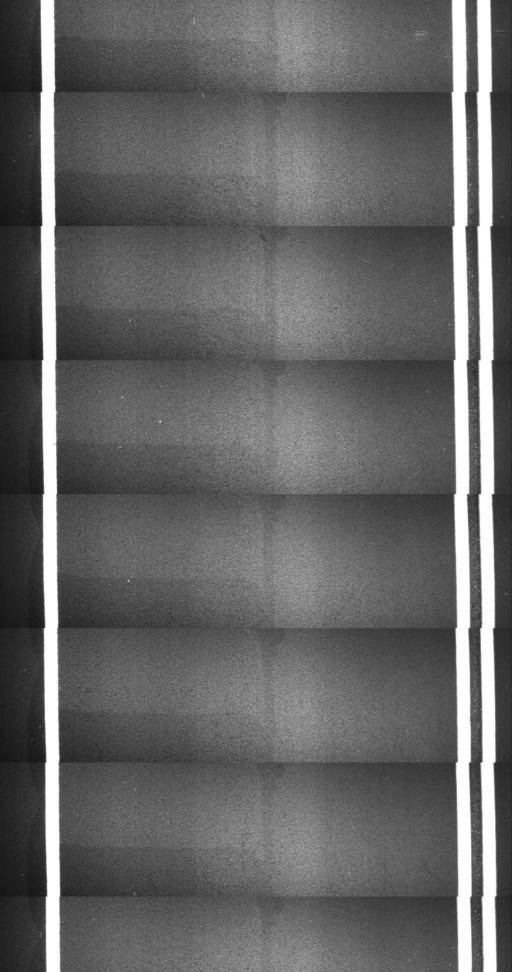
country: US
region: Vermont
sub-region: Caledonia County
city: Lyndonville
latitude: 44.6249
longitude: -71.9044
